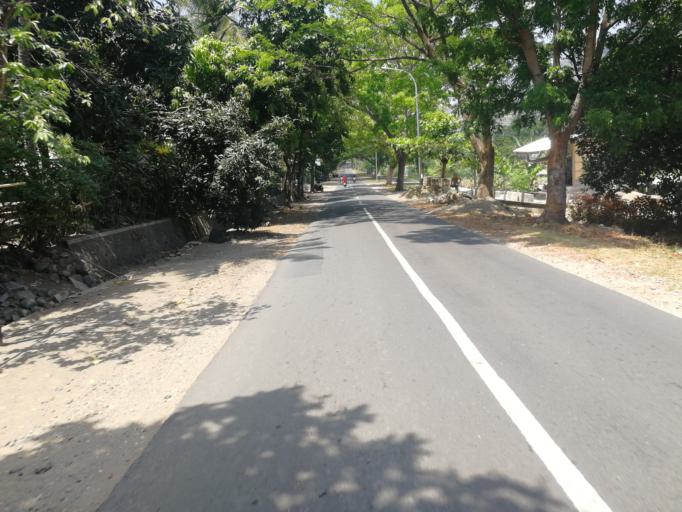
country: ID
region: West Nusa Tenggara
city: Karangsubagan
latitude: -8.4172
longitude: 116.0969
